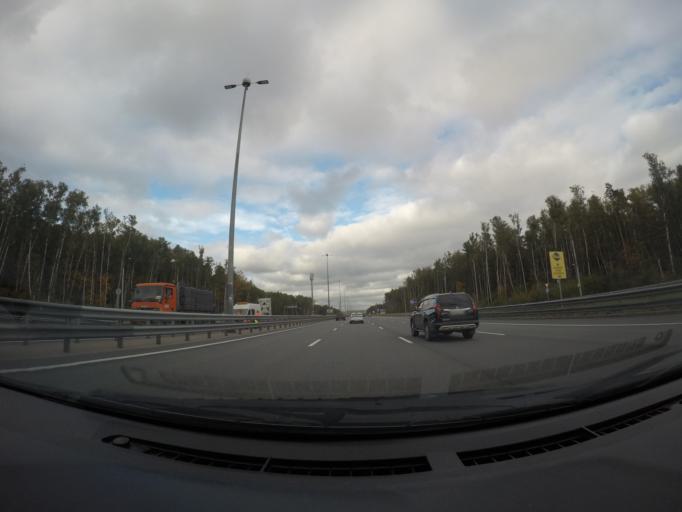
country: RU
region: Moskovskaya
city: Nemchinovka
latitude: 55.7132
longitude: 37.3164
